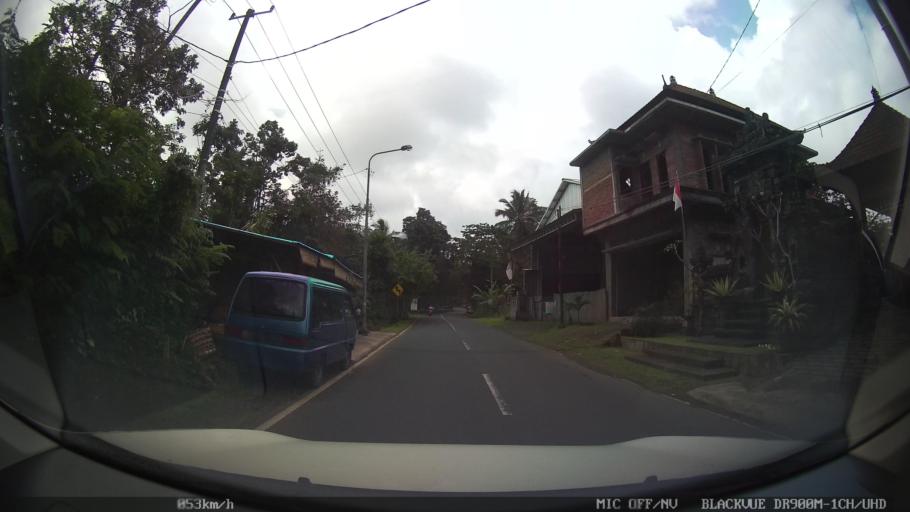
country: ID
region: Bali
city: Petang
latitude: -8.3898
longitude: 115.2195
